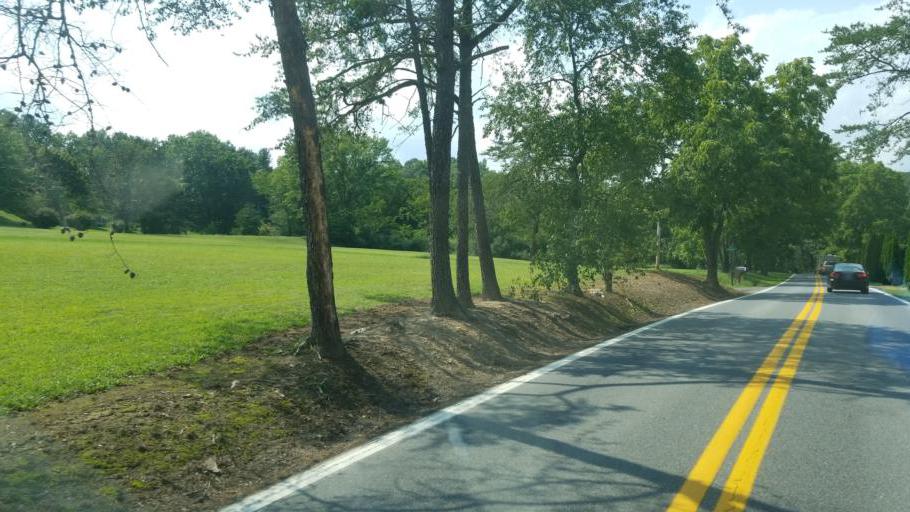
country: US
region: Virginia
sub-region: Frederick County
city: Shawnee Land
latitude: 39.4075
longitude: -78.4322
